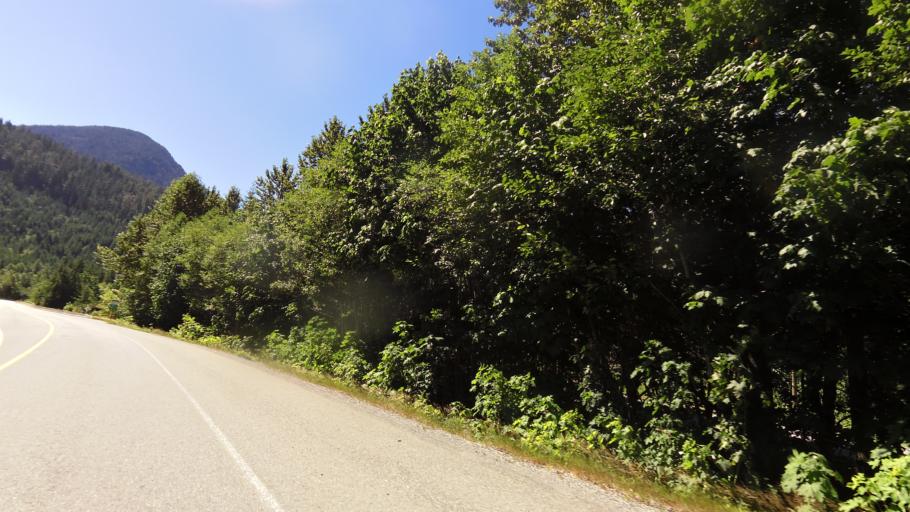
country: CA
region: British Columbia
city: Cumberland
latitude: 49.2980
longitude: -125.2950
